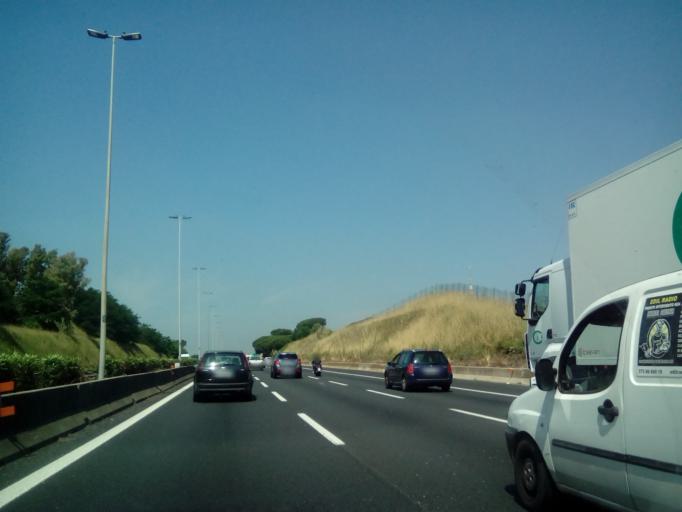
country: IT
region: Latium
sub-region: Citta metropolitana di Roma Capitale
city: Selcetta
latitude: 41.7951
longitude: 12.5011
